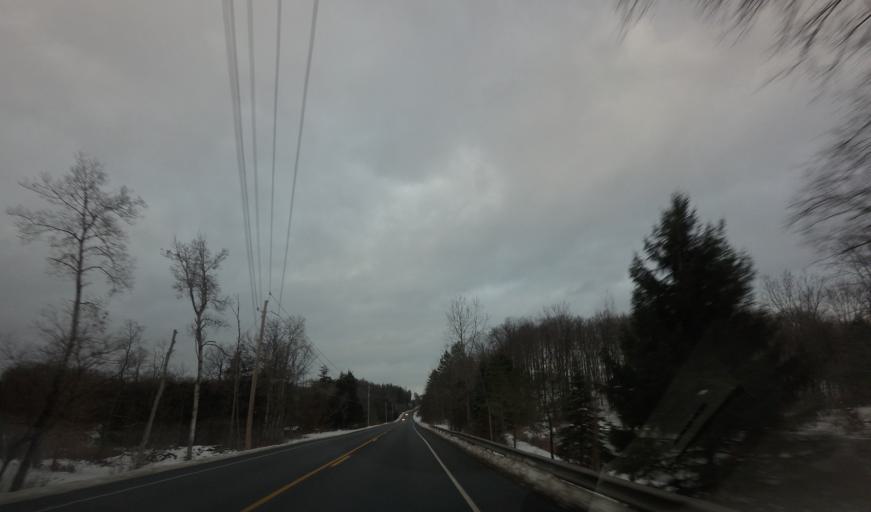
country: US
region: New York
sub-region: Tompkins County
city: Dryden
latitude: 42.5406
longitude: -76.2994
